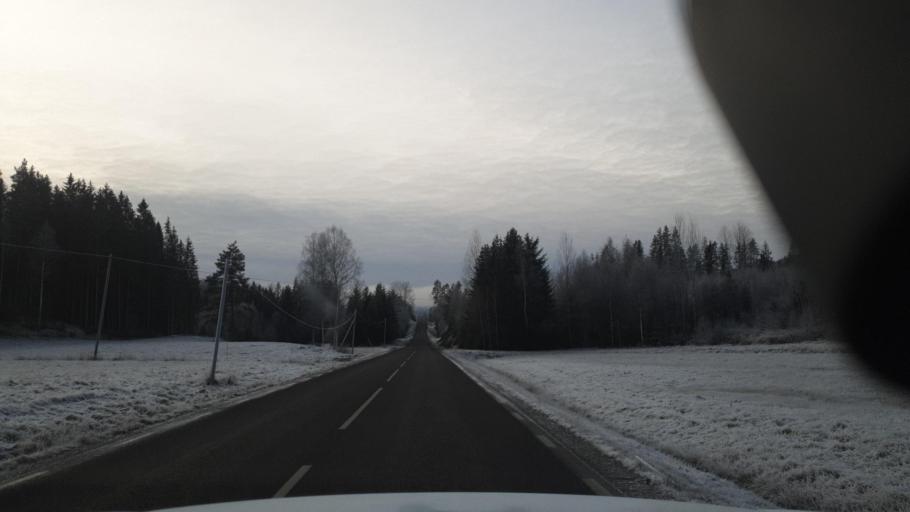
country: SE
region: Vaermland
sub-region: Eda Kommun
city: Amotfors
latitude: 59.6916
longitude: 12.4268
